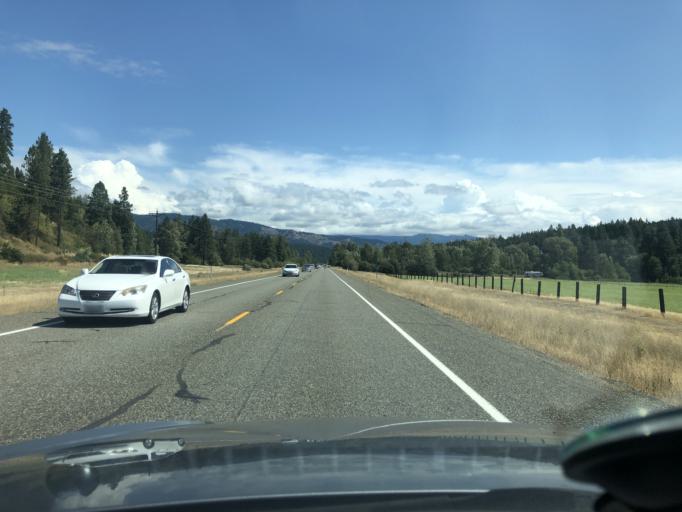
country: US
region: Washington
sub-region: Kittitas County
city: Cle Elum
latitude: 47.1832
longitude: -120.8307
